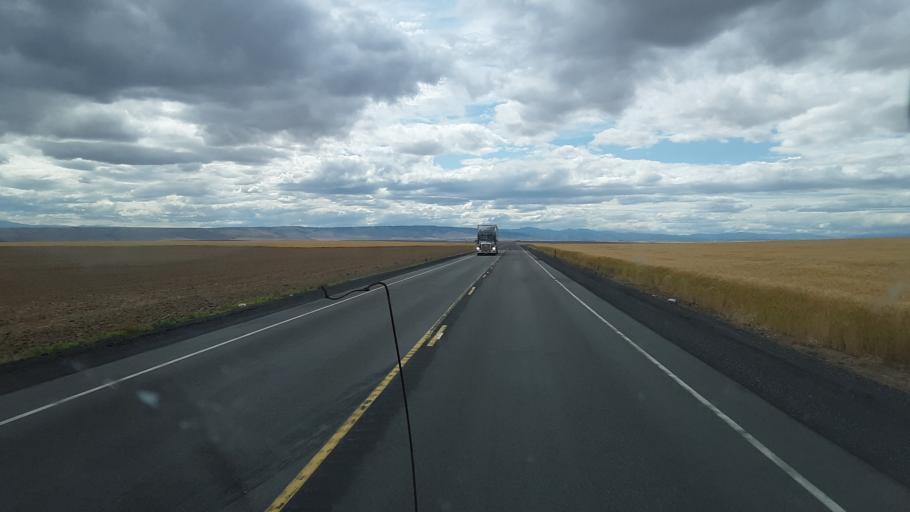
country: US
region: Washington
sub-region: Douglas County
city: Waterville
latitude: 47.6127
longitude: -119.7800
